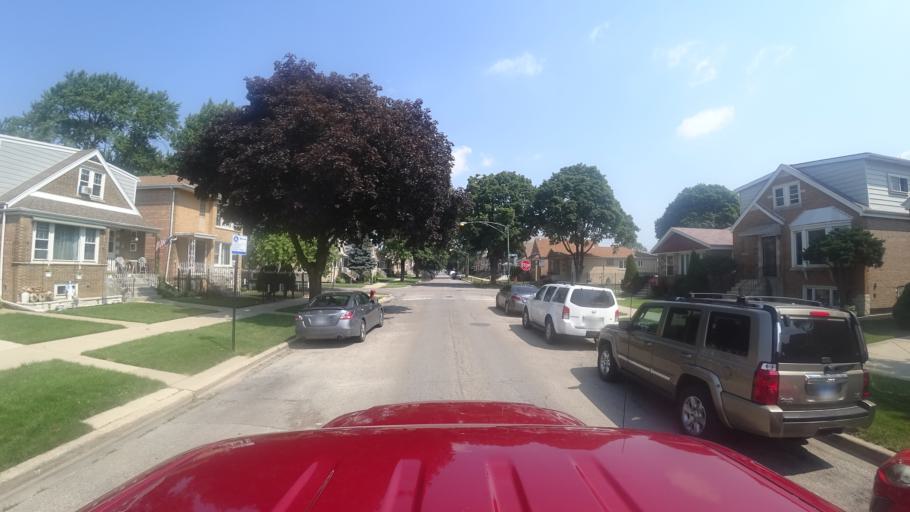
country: US
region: Illinois
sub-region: Cook County
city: Cicero
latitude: 41.8038
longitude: -87.7296
